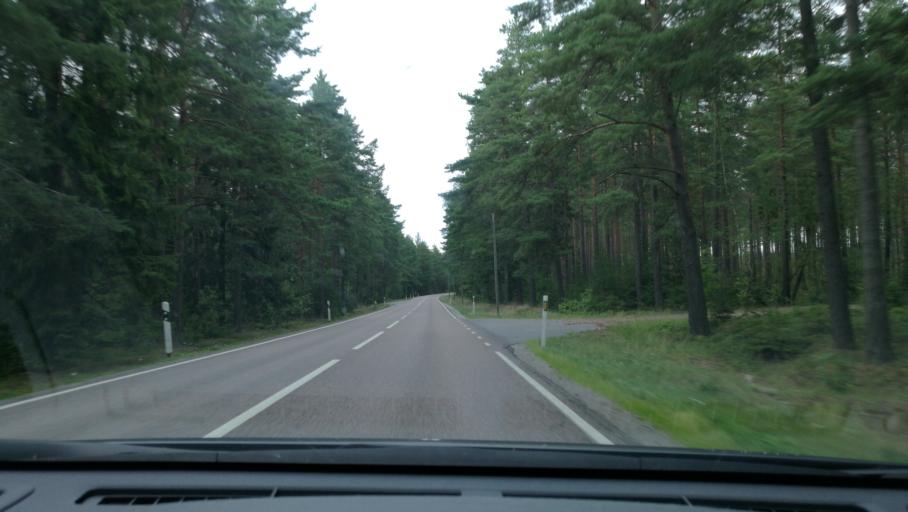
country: SE
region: Vaestmanland
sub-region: Kungsors Kommun
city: Kungsoer
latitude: 59.2998
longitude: 16.1065
